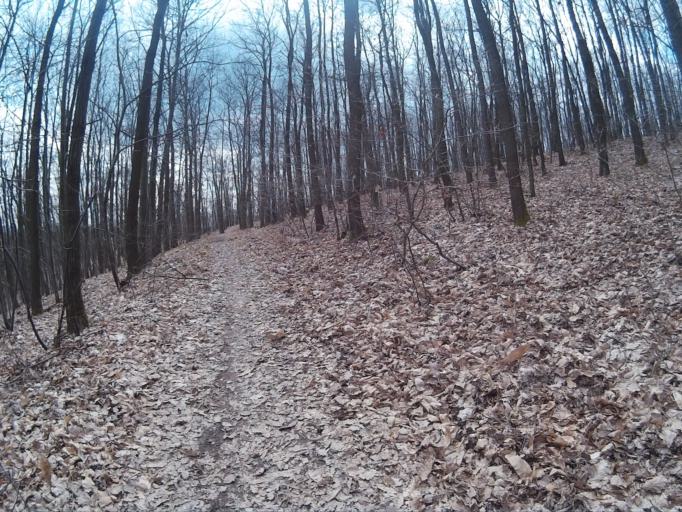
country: HU
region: Pest
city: Kosd
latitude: 47.8288
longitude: 19.1747
